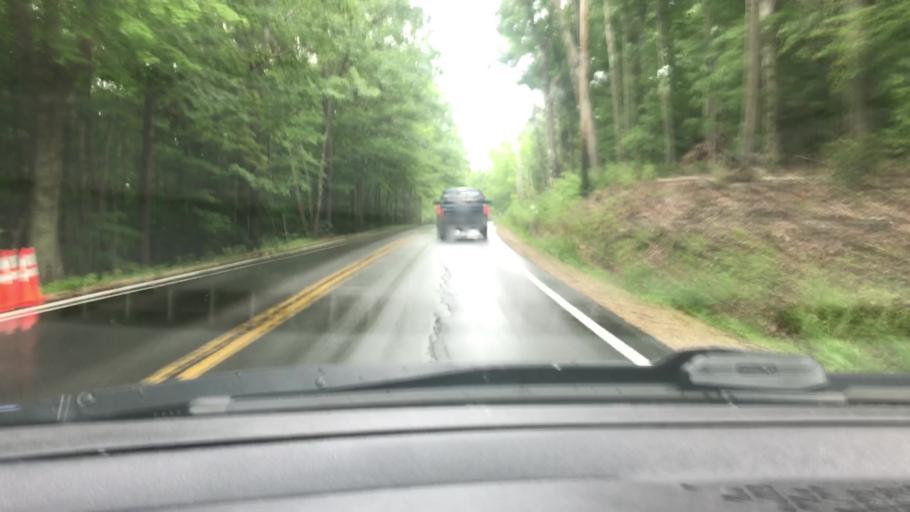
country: US
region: New Hampshire
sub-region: Merrimack County
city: Epsom
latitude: 43.2054
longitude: -71.2759
